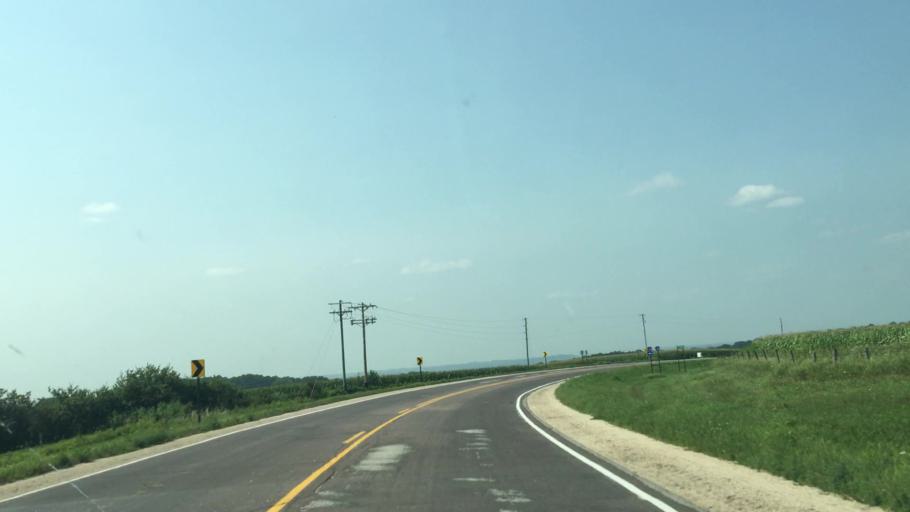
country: US
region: Minnesota
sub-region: Fillmore County
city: Harmony
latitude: 43.6508
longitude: -91.9293
